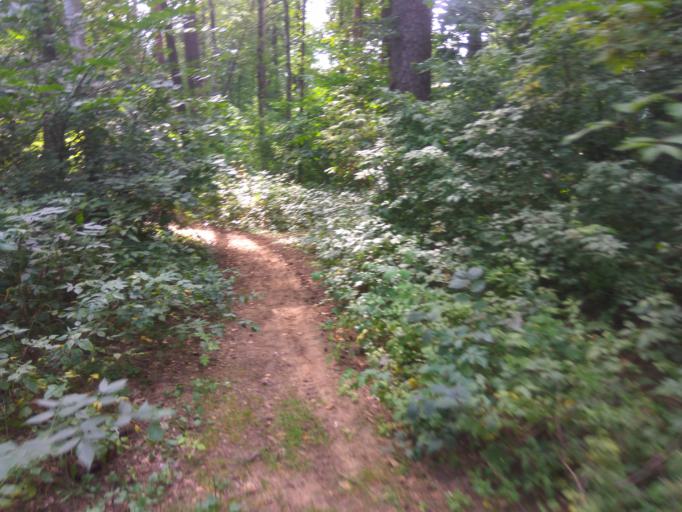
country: RU
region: Moskovskaya
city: Orekhovo-Zuyevo
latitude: 55.8281
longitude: 39.0277
